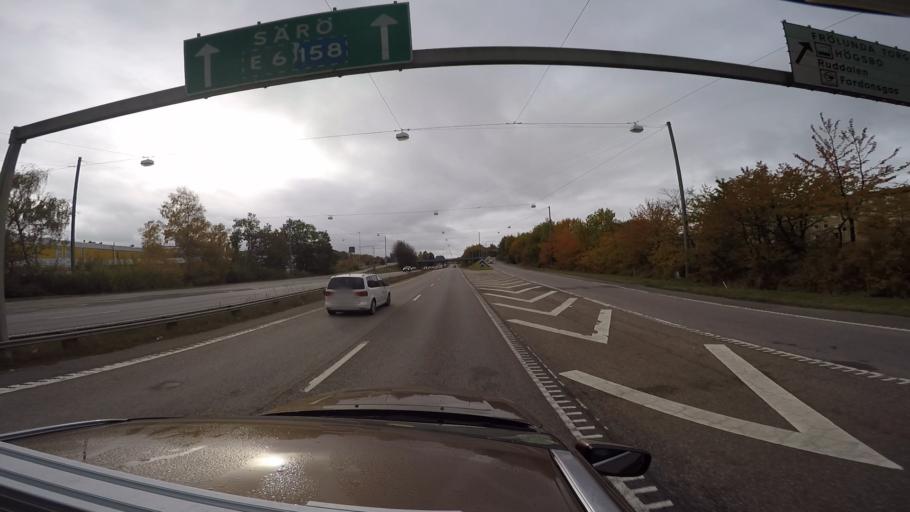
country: SE
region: Vaestra Goetaland
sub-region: Goteborg
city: Majorna
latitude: 57.6620
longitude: 11.9360
